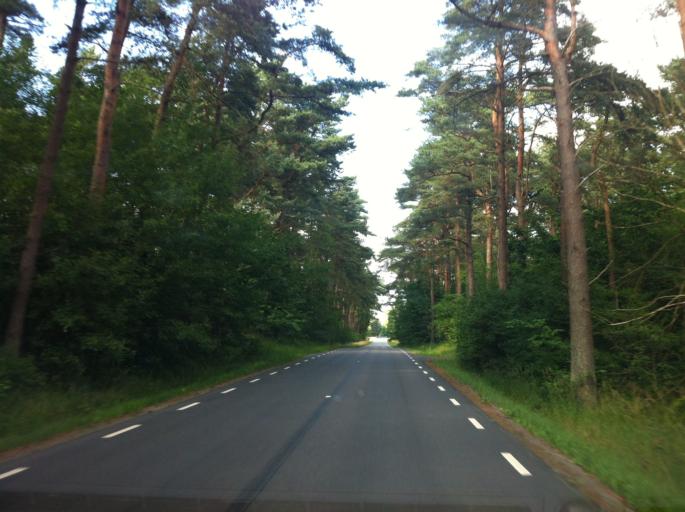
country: SE
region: Skane
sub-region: Simrishamns Kommun
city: Simrishamn
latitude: 55.4465
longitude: 14.2514
